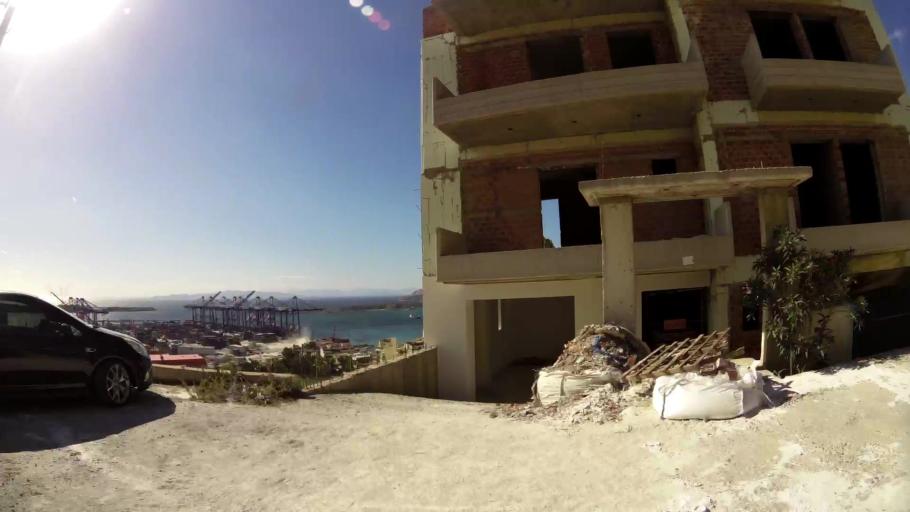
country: GR
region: Attica
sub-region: Nomos Piraios
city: Perama
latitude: 37.9663
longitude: 23.5841
